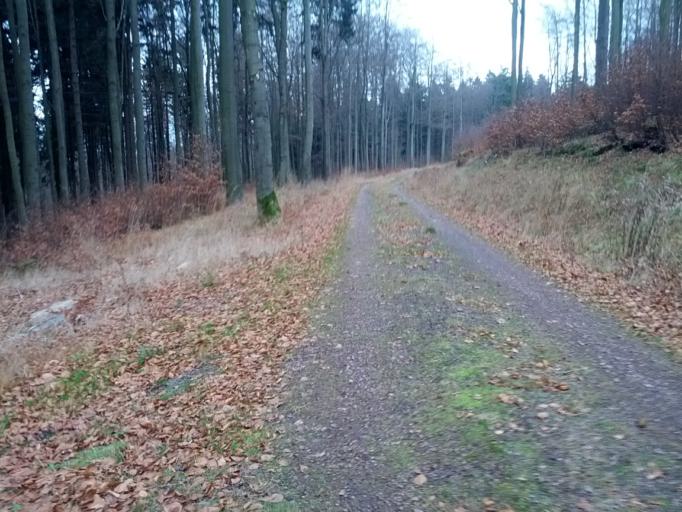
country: DE
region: Thuringia
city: Brotterode
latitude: 50.8556
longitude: 10.4104
